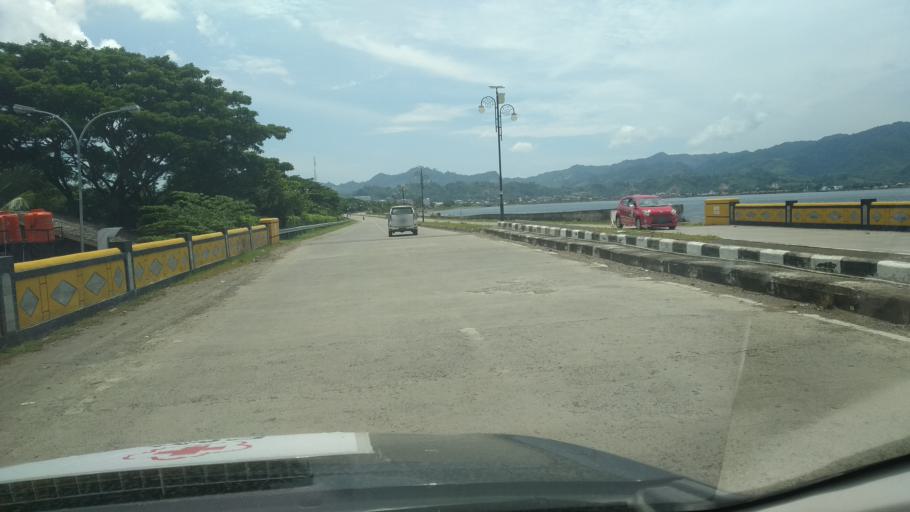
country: ID
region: Sulawesi Barat
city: Mamuju
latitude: -2.6748
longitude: 118.8851
